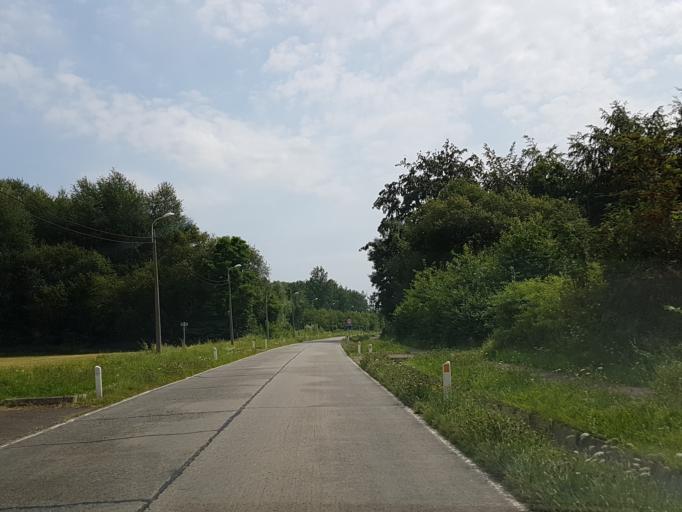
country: BE
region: Flanders
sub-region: Provincie Vlaams-Brabant
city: Herent
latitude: 50.9160
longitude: 4.6382
